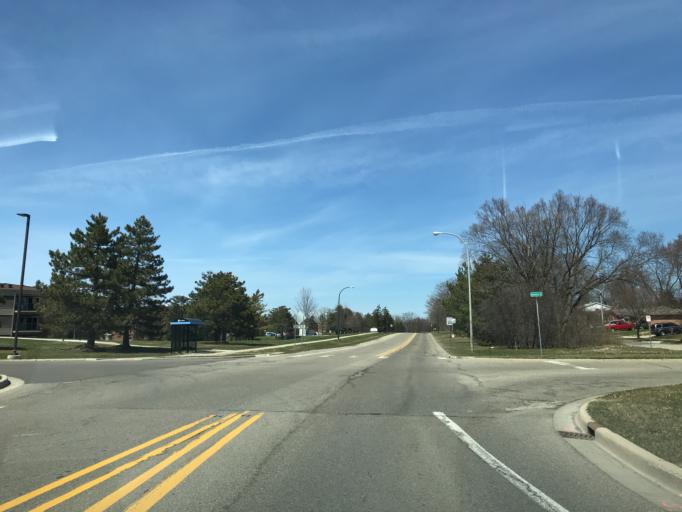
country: US
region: Michigan
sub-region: Washtenaw County
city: Ann Arbor
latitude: 42.3057
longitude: -83.7076
